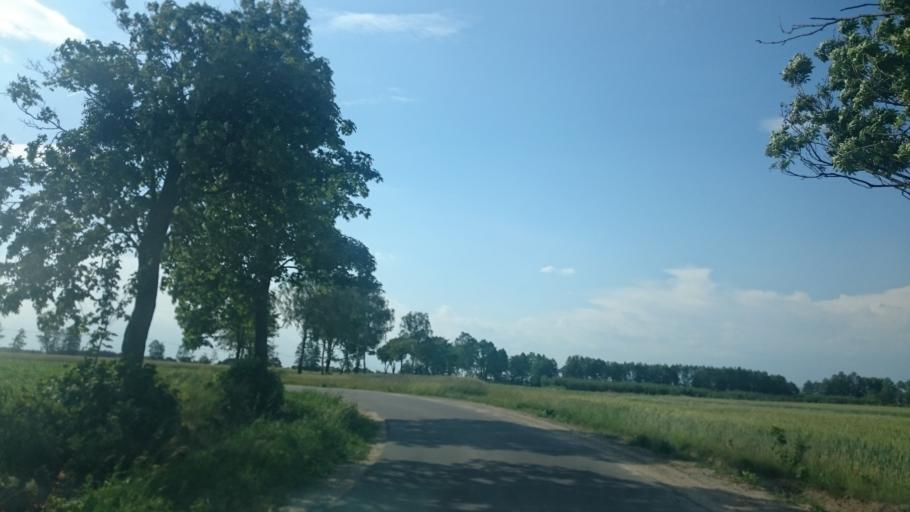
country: PL
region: Kujawsko-Pomorskie
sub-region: Powiat golubsko-dobrzynski
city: Radomin
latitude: 53.1144
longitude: 19.1406
